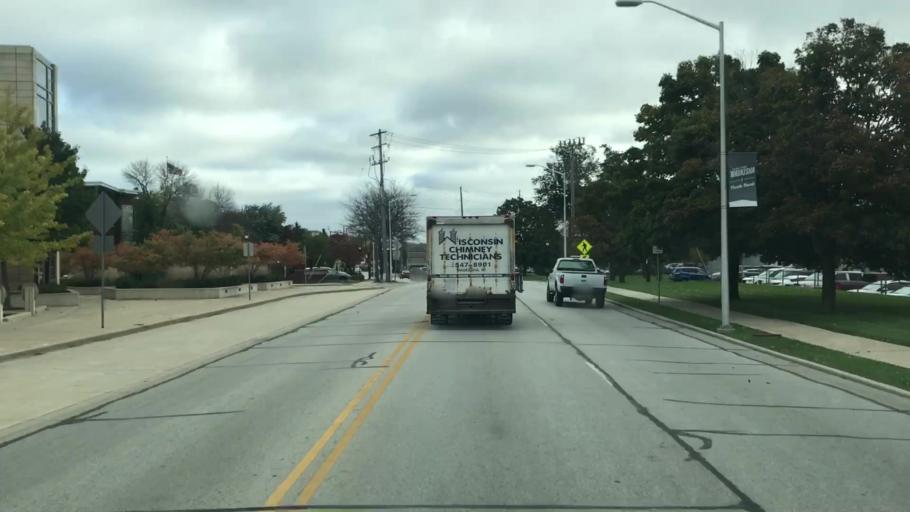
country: US
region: Wisconsin
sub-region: Waukesha County
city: Waukesha
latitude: 43.0134
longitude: -88.2329
